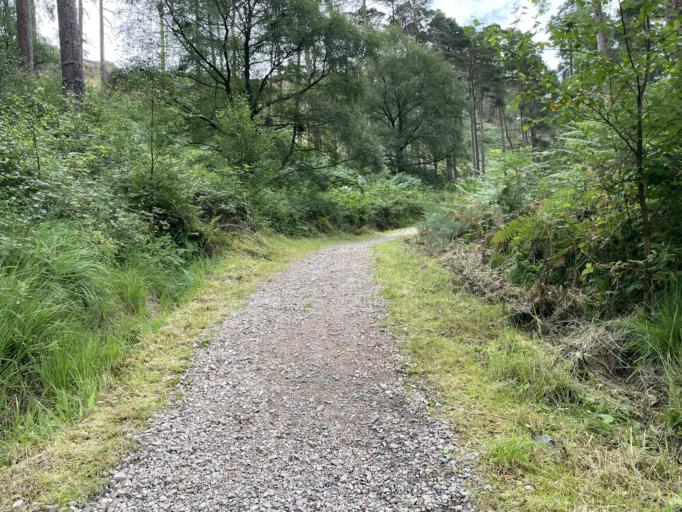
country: GB
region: Scotland
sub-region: Dumfries and Galloway
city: Newton Stewart
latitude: 55.0894
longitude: -4.4705
